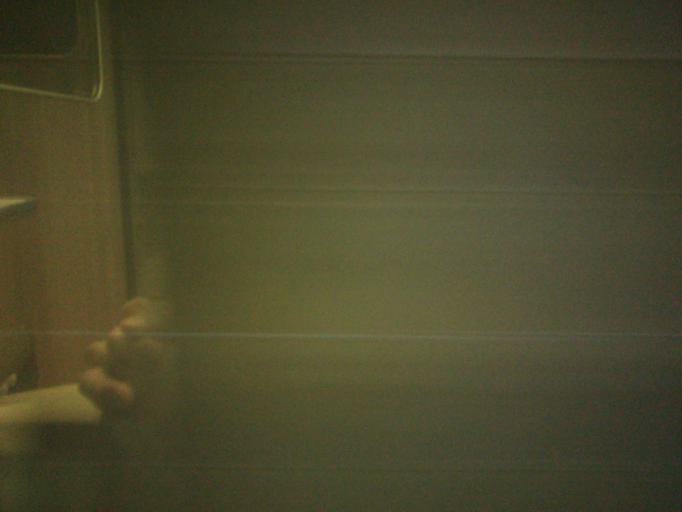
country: JP
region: Kochi
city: Susaki
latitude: 33.3265
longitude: 133.2258
